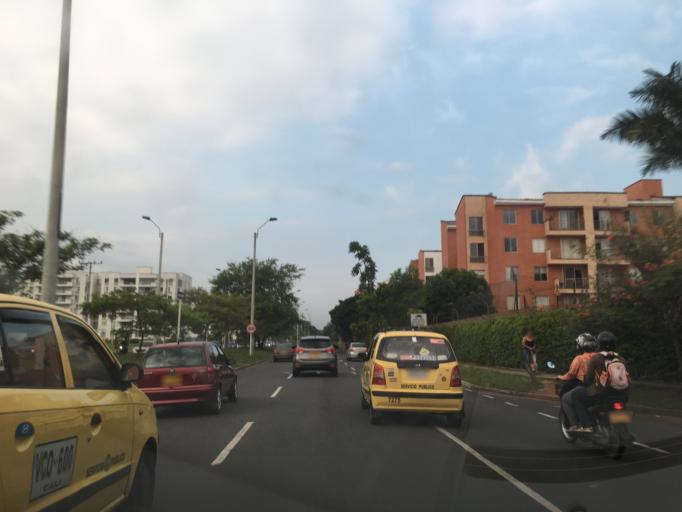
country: CO
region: Valle del Cauca
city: Cali
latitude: 3.3957
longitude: -76.5281
